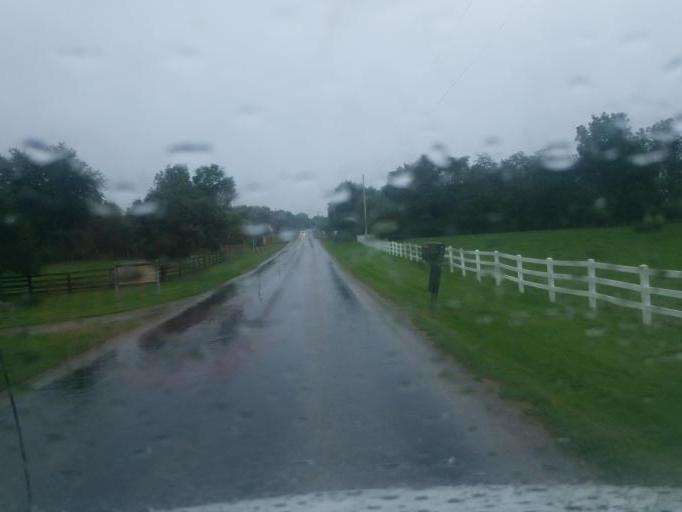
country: US
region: Ohio
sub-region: Wayne County
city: Creston
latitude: 40.9748
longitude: -81.9132
